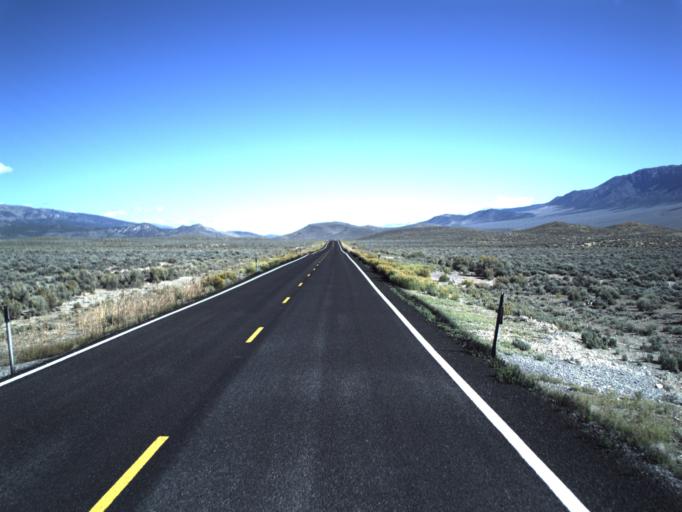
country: US
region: Utah
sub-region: Piute County
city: Junction
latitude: 38.2126
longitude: -112.0030
